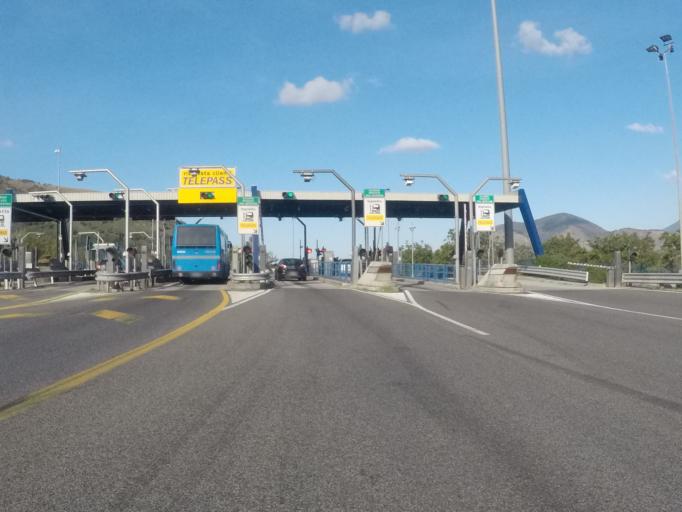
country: IT
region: Campania
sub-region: Provincia di Salerno
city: Piazza del Galdo-Sant'Angelo
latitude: 40.7728
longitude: 14.7277
